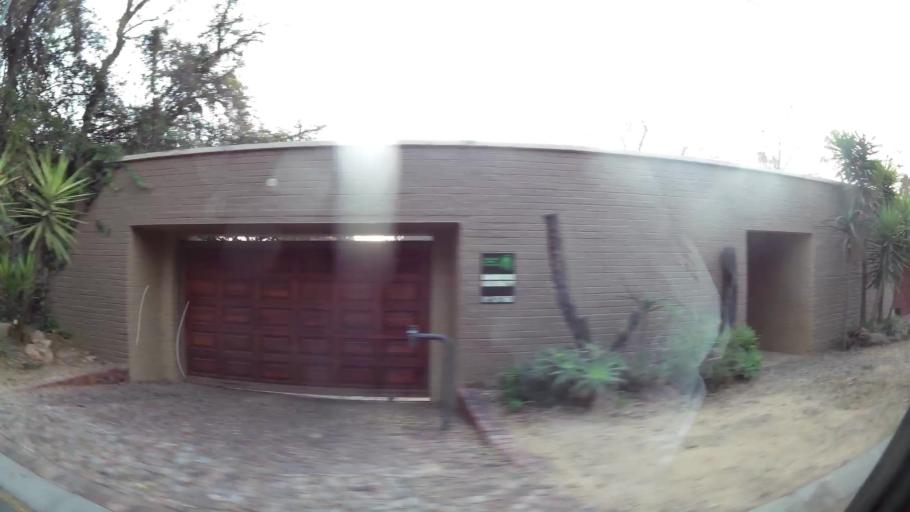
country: ZA
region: Gauteng
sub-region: City of Johannesburg Metropolitan Municipality
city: Diepsloot
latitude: -26.0404
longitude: 27.9861
